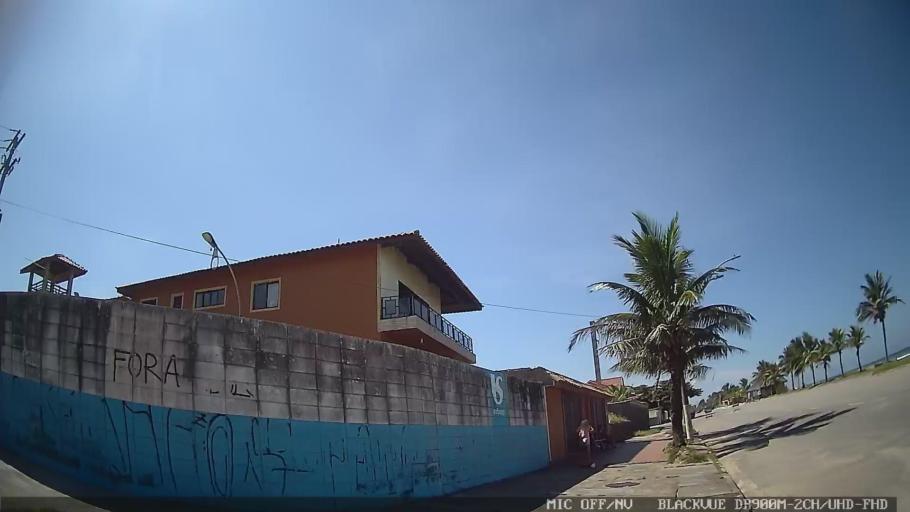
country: BR
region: Sao Paulo
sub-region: Peruibe
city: Peruibe
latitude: -24.3037
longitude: -46.9723
